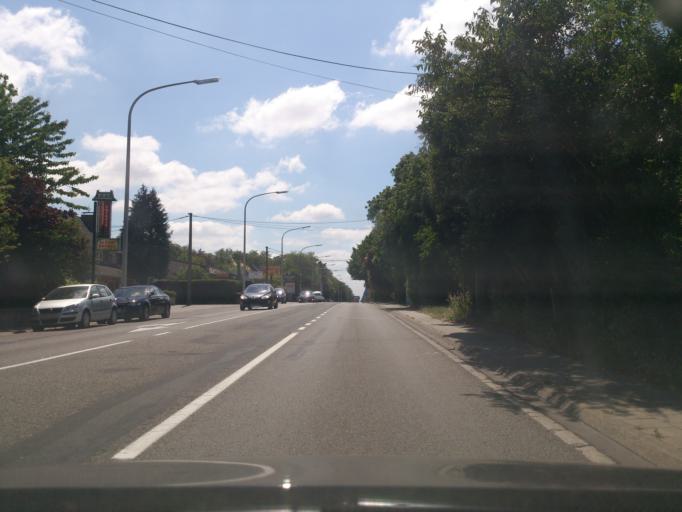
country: BE
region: Wallonia
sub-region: Province du Brabant Wallon
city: Waterloo
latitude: 50.6843
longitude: 4.4019
